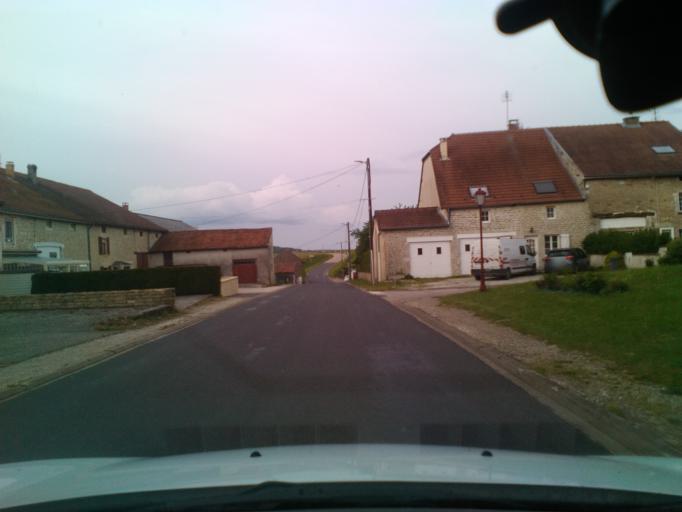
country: FR
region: Champagne-Ardenne
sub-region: Departement de la Haute-Marne
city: Doulaincourt-Saucourt
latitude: 48.2236
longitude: 5.2597
